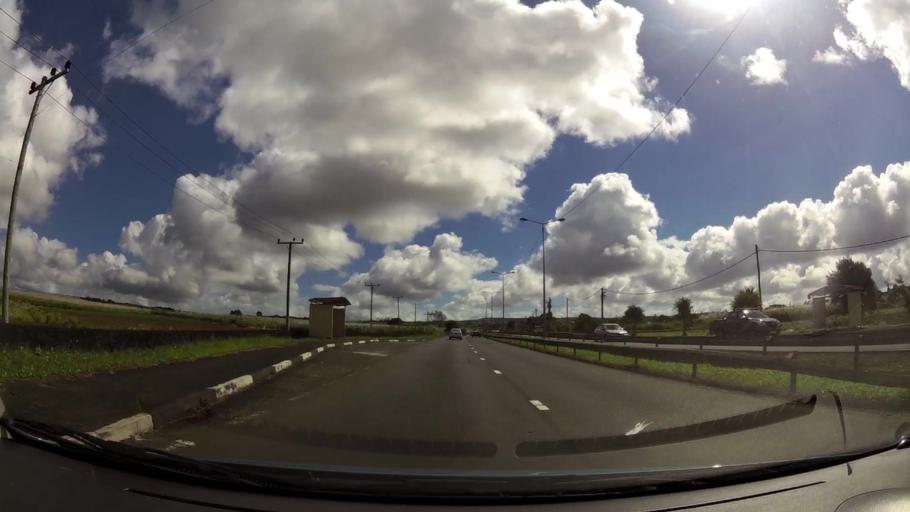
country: MU
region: Grand Port
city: Rose Belle
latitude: -20.3993
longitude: 57.5856
